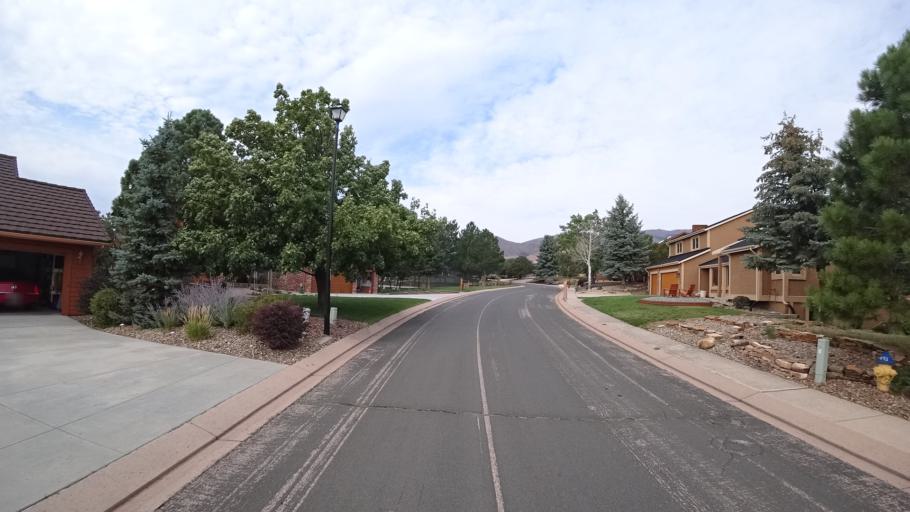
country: US
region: Colorado
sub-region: El Paso County
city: Air Force Academy
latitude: 38.9376
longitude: -104.8609
